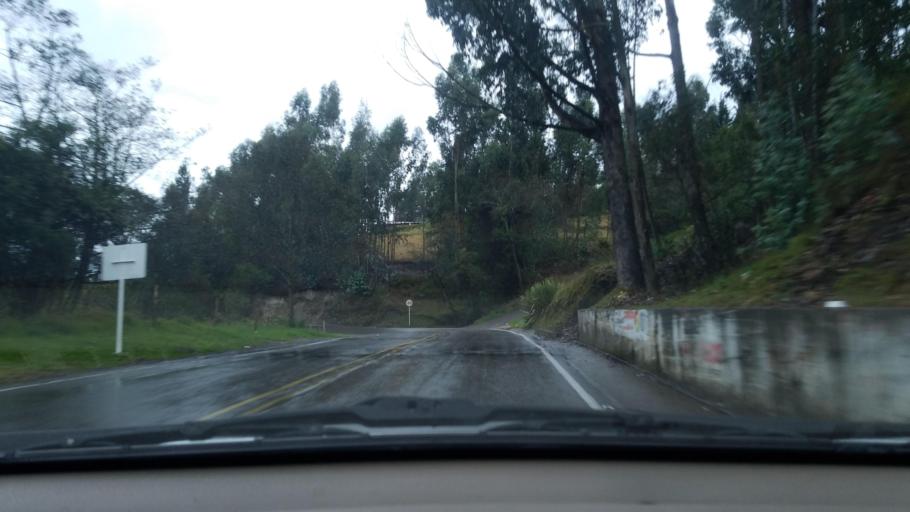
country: CO
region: Boyaca
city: Firavitoba
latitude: 5.6280
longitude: -72.9212
